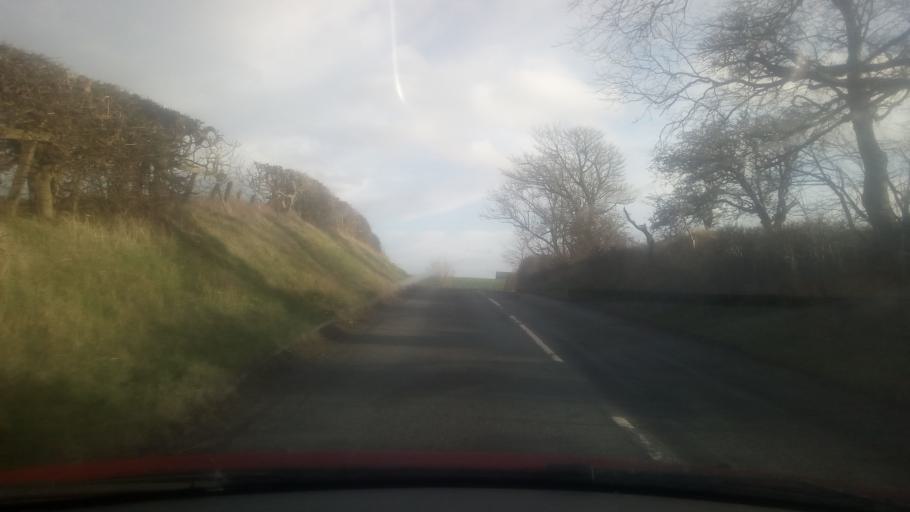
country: GB
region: Scotland
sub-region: The Scottish Borders
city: Coldstream
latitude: 55.7125
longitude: -2.2815
